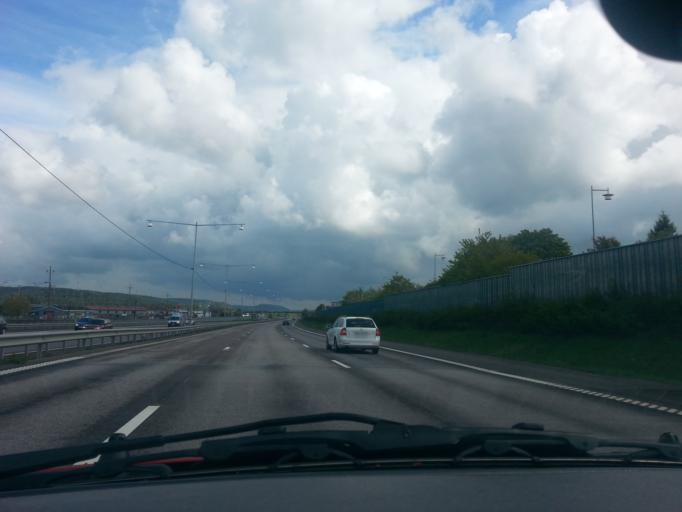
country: SE
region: Vaestra Goetaland
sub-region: Goteborg
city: Eriksbo
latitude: 57.7306
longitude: 12.0555
